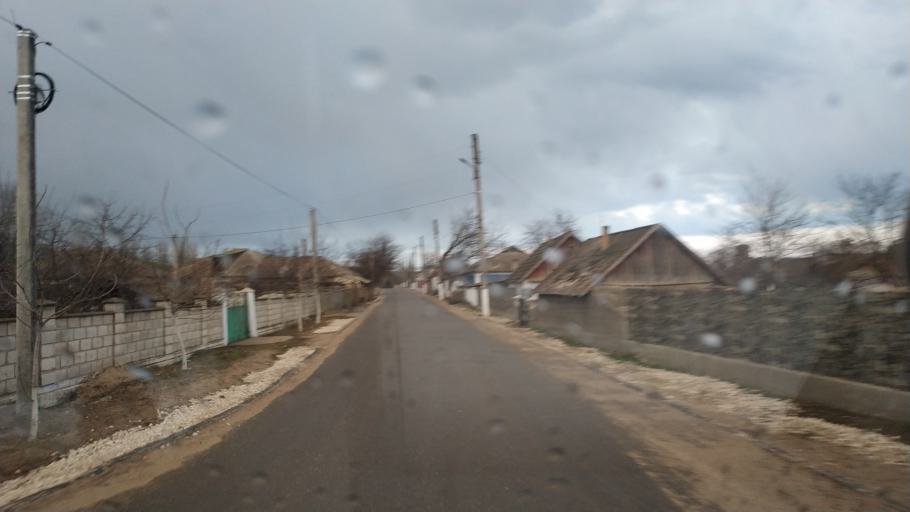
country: MD
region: Telenesti
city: Grigoriopol
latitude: 47.0865
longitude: 29.3446
